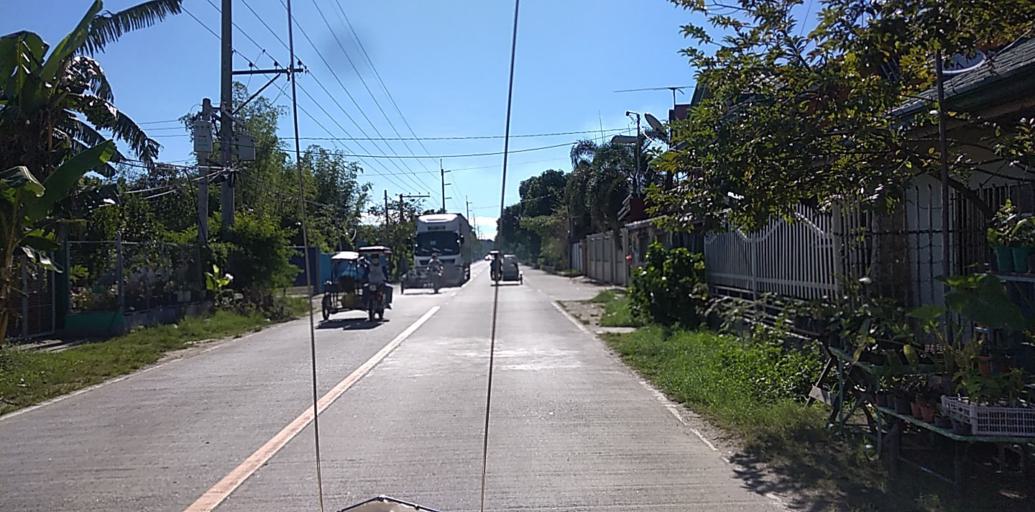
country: PH
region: Central Luzon
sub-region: Province of Pampanga
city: Santo Domingo
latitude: 15.0715
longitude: 120.7624
